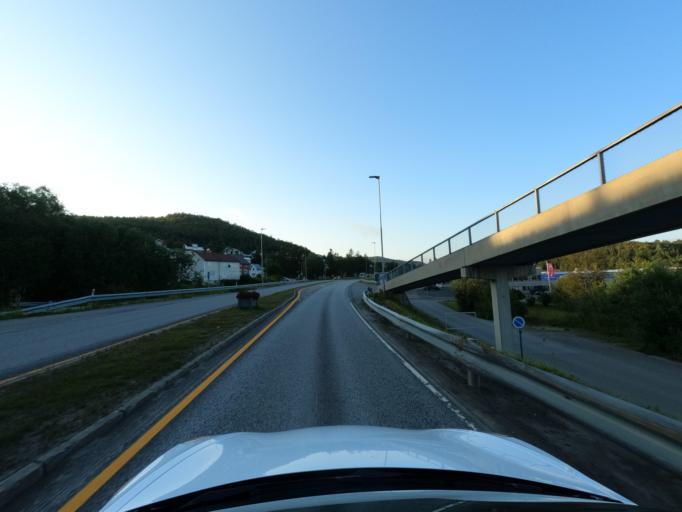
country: NO
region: Troms
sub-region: Harstad
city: Harstad
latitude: 68.7713
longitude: 16.5578
